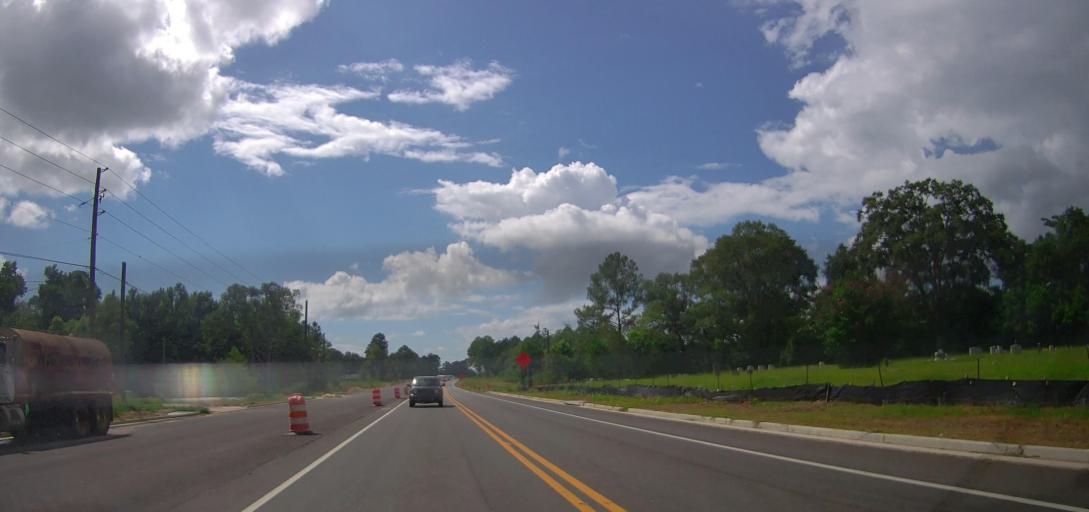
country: US
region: Georgia
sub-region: Coffee County
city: Douglas
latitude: 31.5263
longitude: -82.9037
